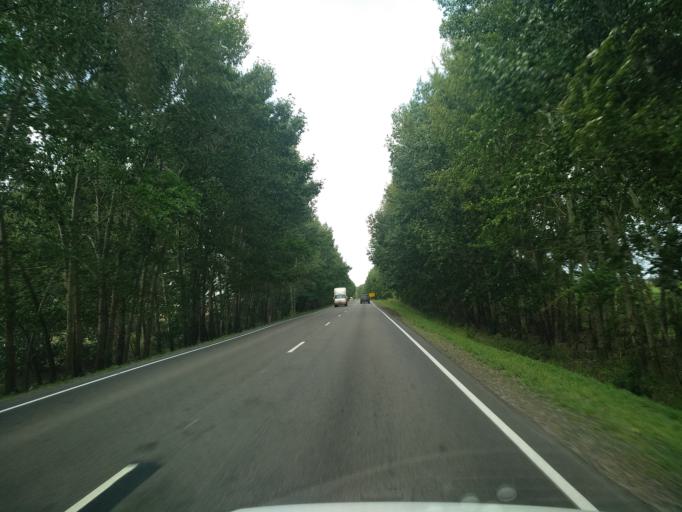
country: RU
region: Voronezj
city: Pereleshino
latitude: 51.8026
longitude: 40.1695
